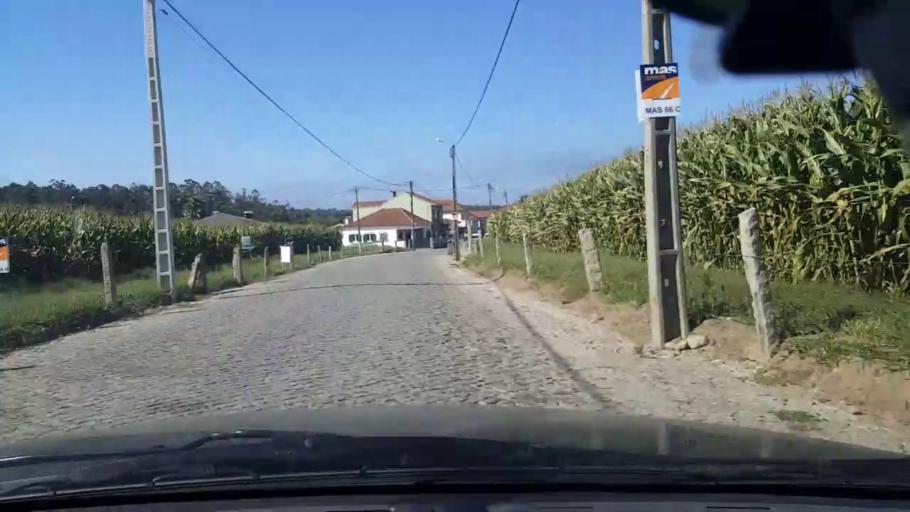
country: PT
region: Porto
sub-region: Maia
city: Gemunde
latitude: 41.2806
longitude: -8.6612
